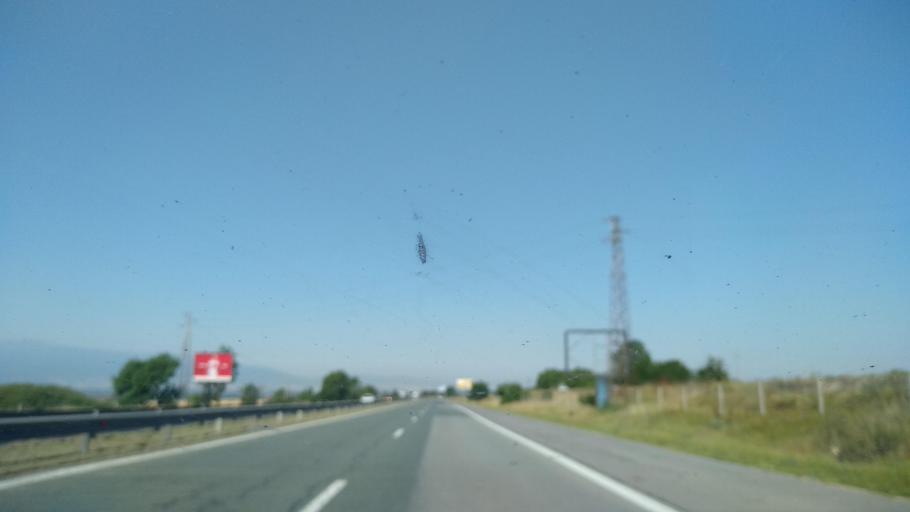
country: BG
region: Sofia-Capital
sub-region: Stolichna Obshtina
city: Bukhovo
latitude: 42.7314
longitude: 23.5890
